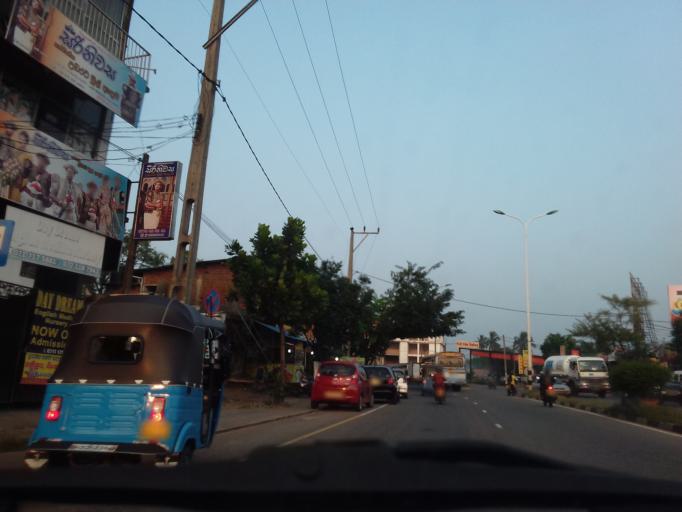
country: LK
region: Western
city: Kelaniya
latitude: 6.9913
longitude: 79.9408
